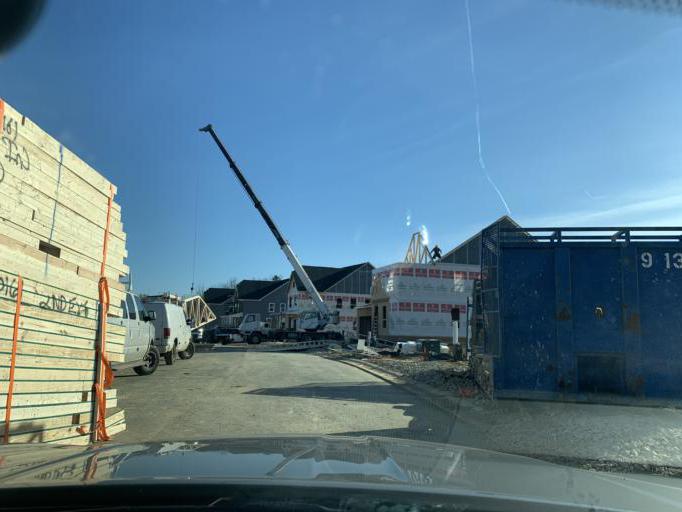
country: US
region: Maryland
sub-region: Anne Arundel County
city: Crofton
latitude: 39.0207
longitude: -76.7284
